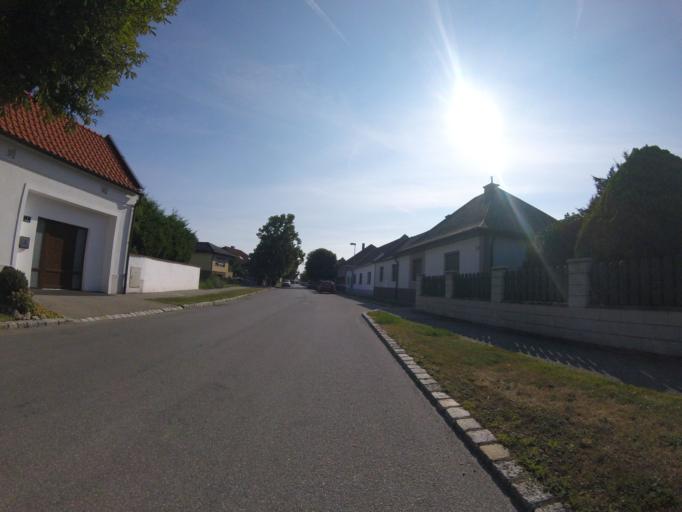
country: AT
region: Burgenland
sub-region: Politischer Bezirk Neusiedl am See
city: Illmitz
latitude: 47.7623
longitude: 16.8057
